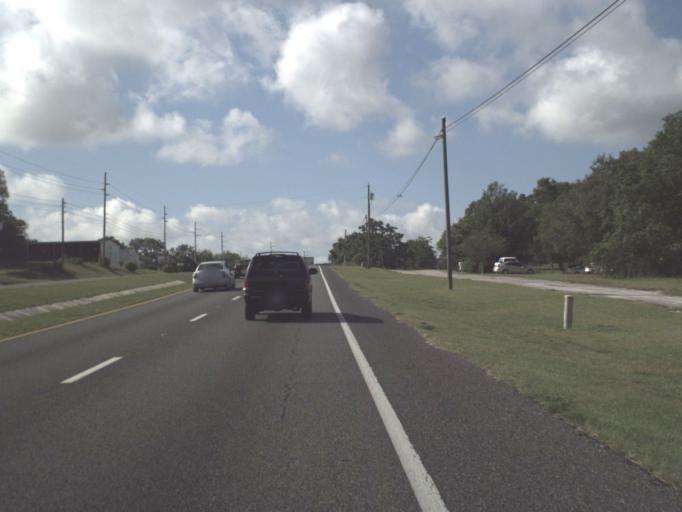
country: US
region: Florida
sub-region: Lake County
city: Lady Lake
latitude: 28.8937
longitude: -81.9085
